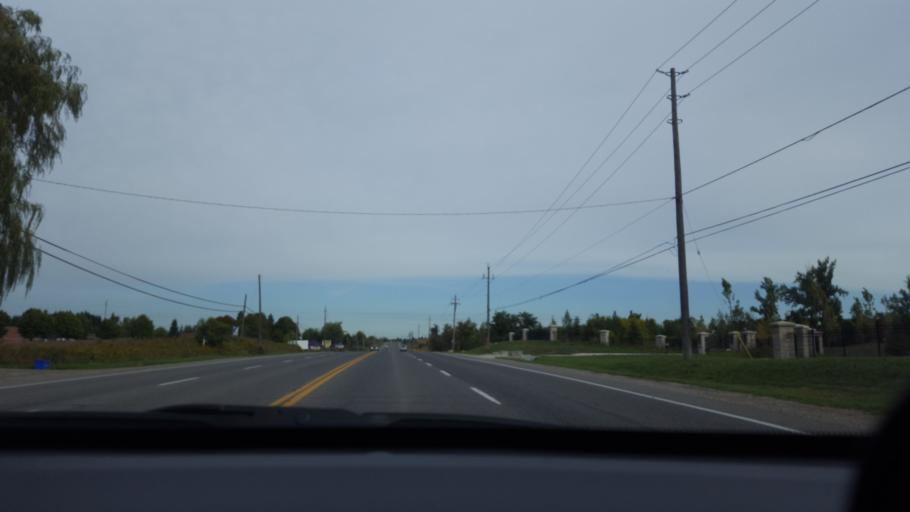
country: CA
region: Ontario
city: Vaughan
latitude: 43.8957
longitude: -79.5218
